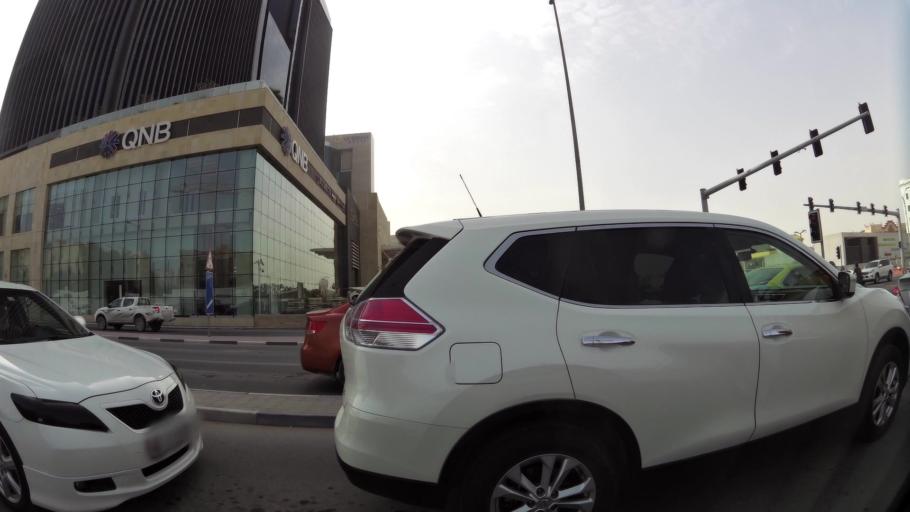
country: QA
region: Baladiyat ad Dawhah
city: Doha
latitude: 25.2818
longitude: 51.5068
